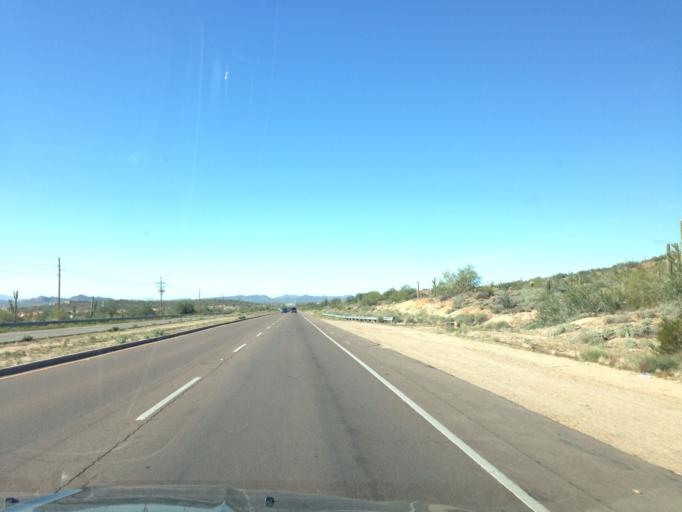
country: US
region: Arizona
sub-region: Maricopa County
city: Anthem
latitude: 33.7986
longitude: -112.1017
